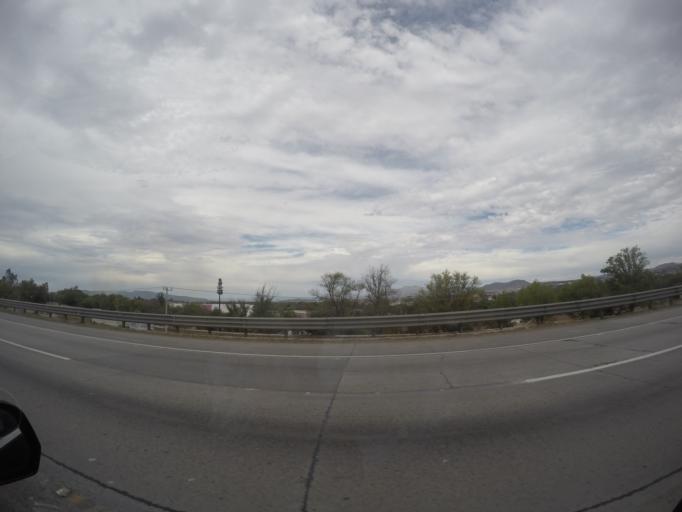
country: MX
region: Queretaro
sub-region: San Juan del Rio
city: Vista Hermosa (Cuasinada)
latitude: 20.3814
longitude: -100.0135
